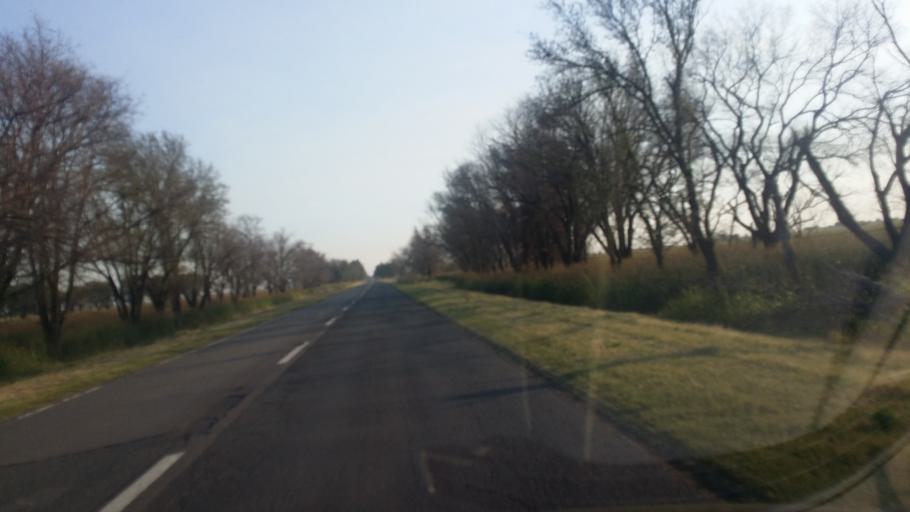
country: AR
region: La Pampa
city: Winifreda
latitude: -36.1955
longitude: -64.2781
